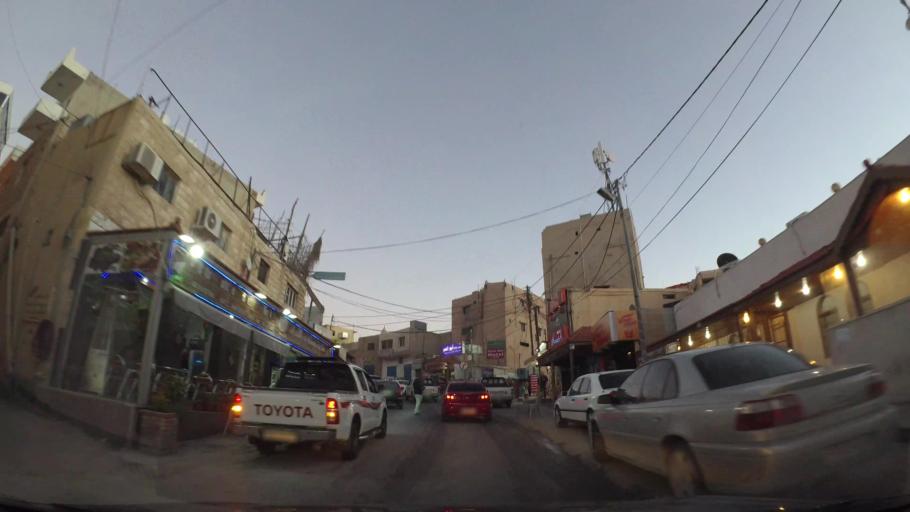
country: JO
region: Ma'an
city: Petra
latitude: 30.3211
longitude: 35.4789
